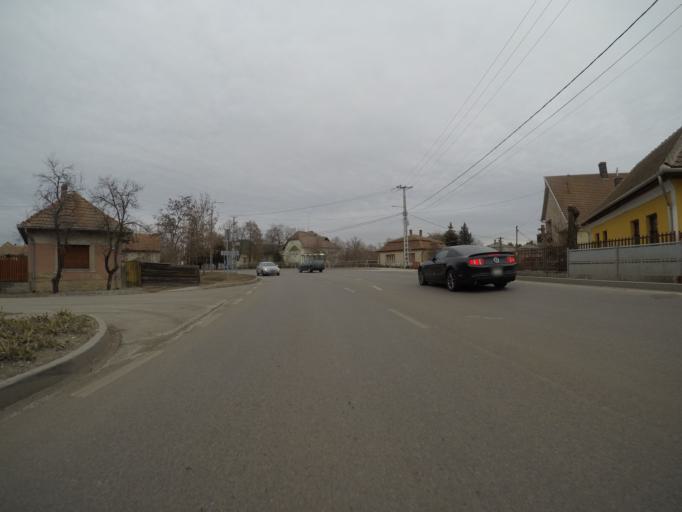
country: HU
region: Jasz-Nagykun-Szolnok
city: Jaszjakohalma
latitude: 47.5176
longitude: 19.9830
